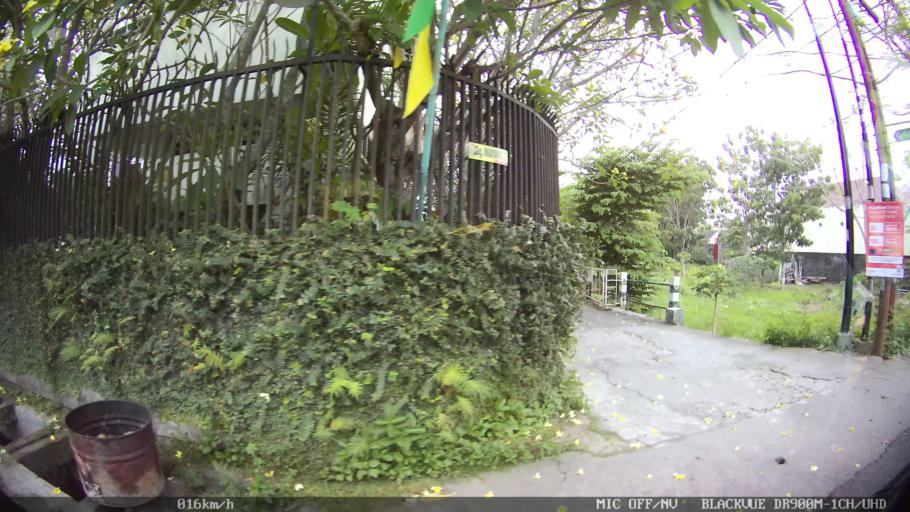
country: ID
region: Daerah Istimewa Yogyakarta
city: Yogyakarta
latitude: -7.8158
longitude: 110.4044
